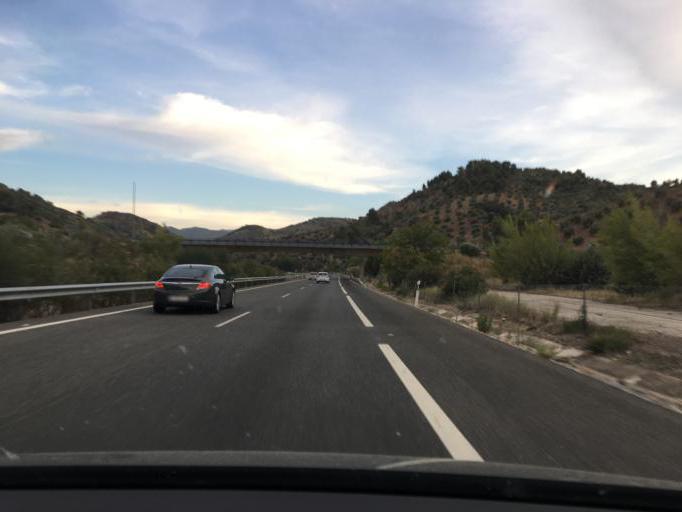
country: ES
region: Andalusia
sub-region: Provincia de Jaen
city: Cambil
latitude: 37.6769
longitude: -3.6251
